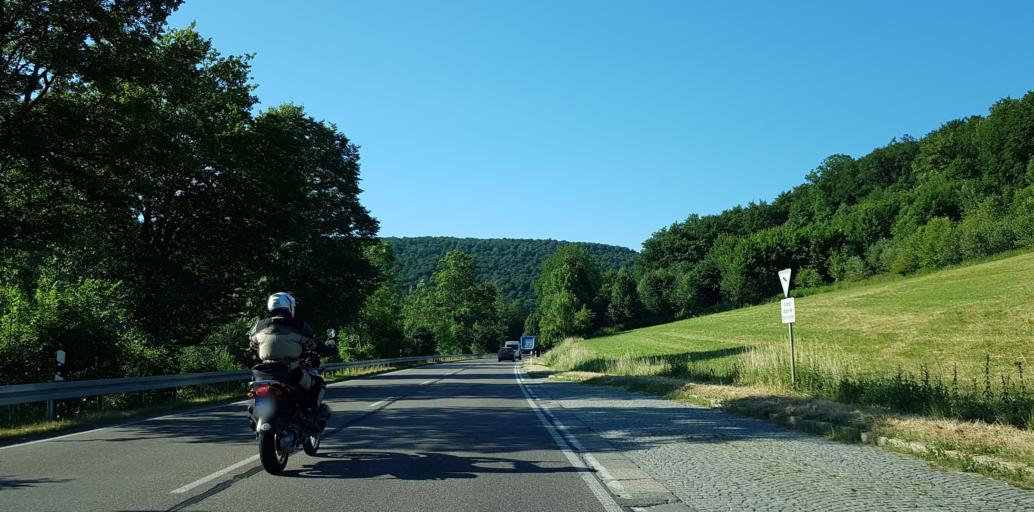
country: DE
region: Baden-Wuerttemberg
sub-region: Tuebingen Region
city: Blaubeuren
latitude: 48.3941
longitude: 9.7677
